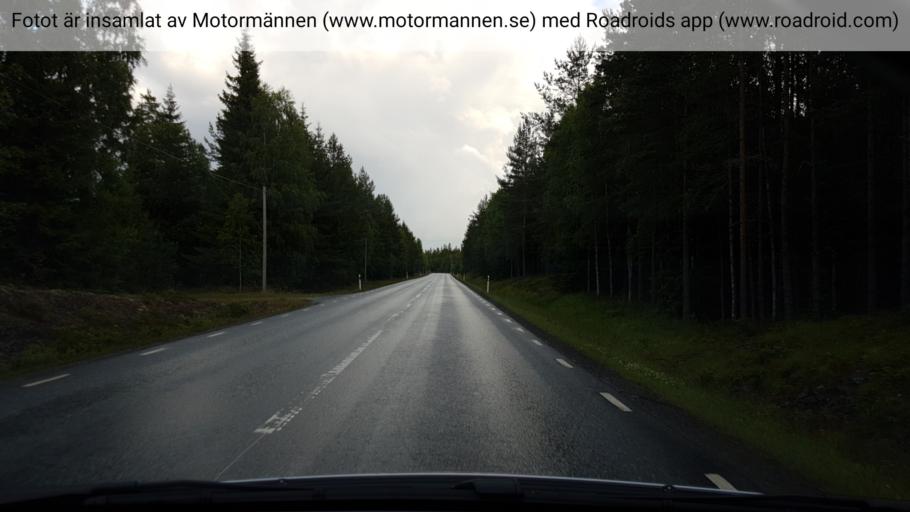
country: SE
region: OErebro
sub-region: Nora Kommun
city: As
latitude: 59.5498
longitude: 14.7584
